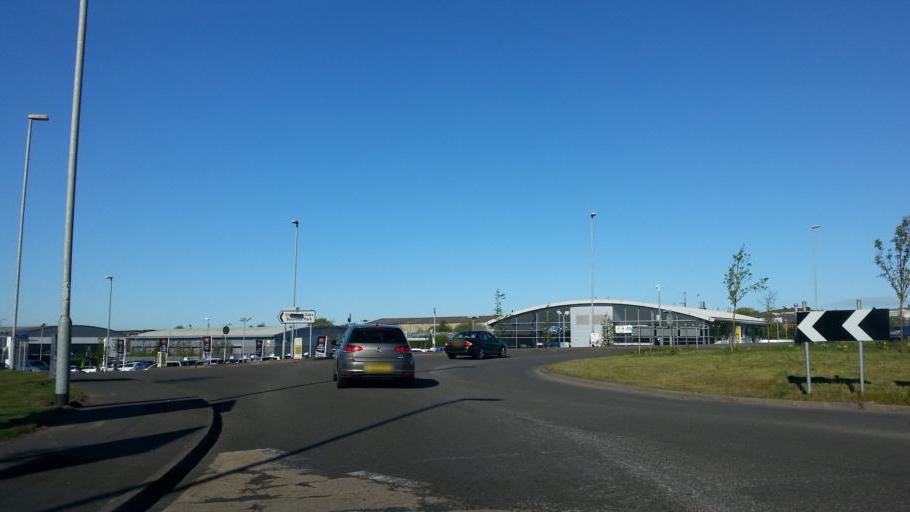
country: GB
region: England
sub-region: Nottinghamshire
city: Rainworth
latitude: 53.1271
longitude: -1.1490
